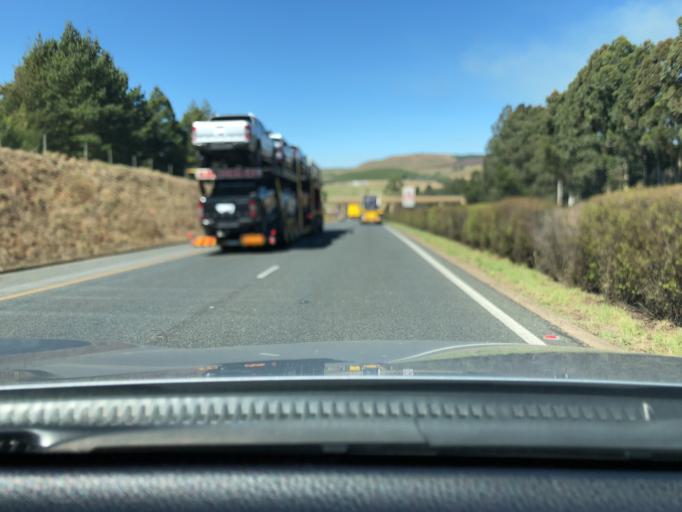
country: ZA
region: KwaZulu-Natal
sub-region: uMgungundlovu District Municipality
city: Mooirivier
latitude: -29.3515
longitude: 30.0875
